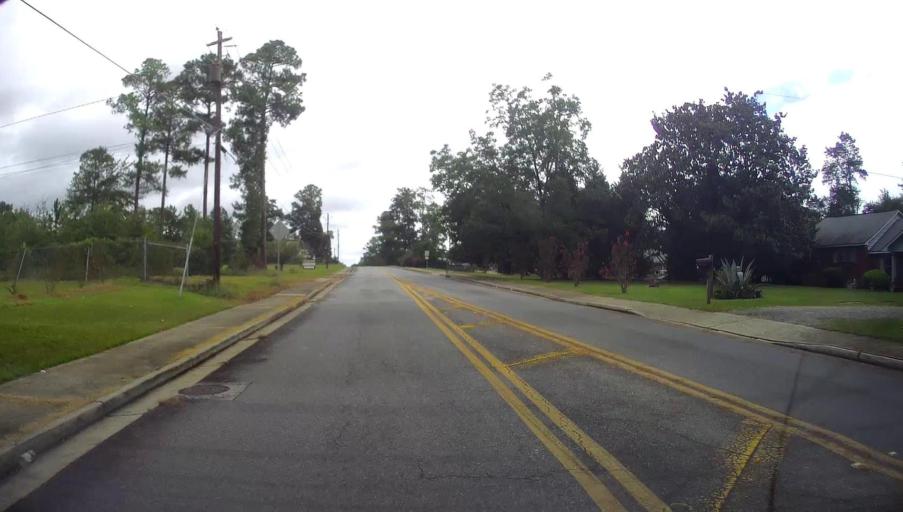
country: US
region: Georgia
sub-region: Bibb County
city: Macon
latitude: 32.8039
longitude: -83.7003
